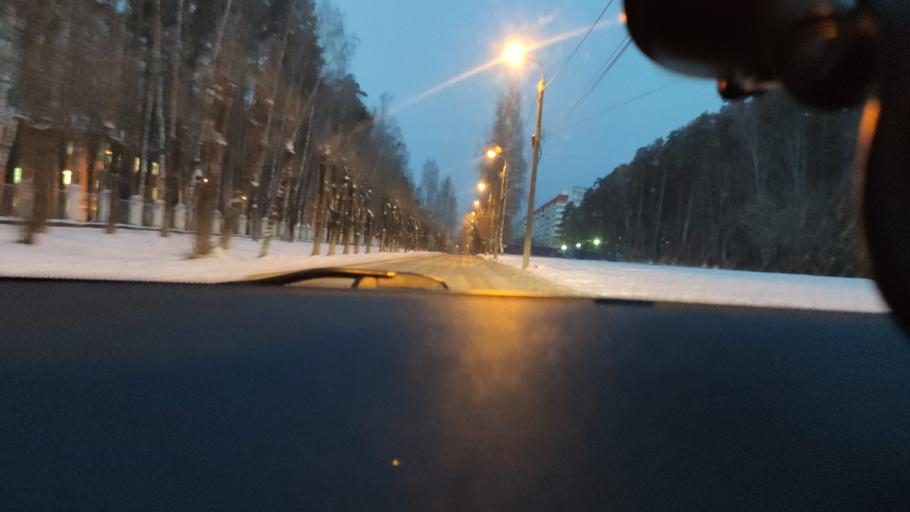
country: RU
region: Perm
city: Kultayevo
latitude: 58.0095
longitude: 55.9628
